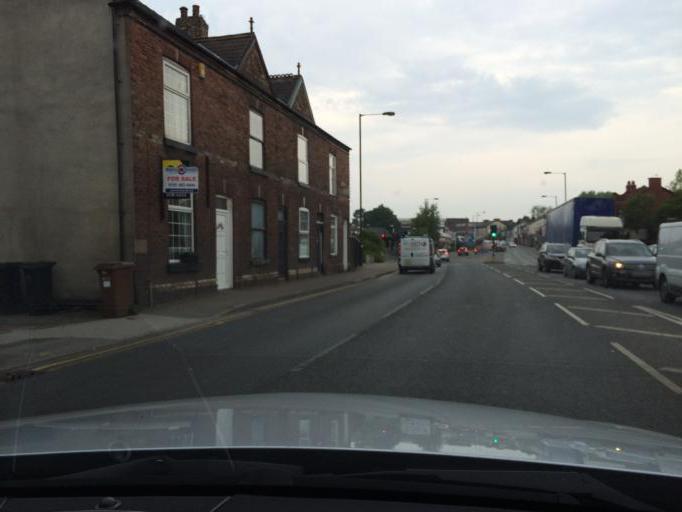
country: GB
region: England
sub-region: Borough of Stockport
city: Hazel Grove
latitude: 53.3774
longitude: -2.1164
